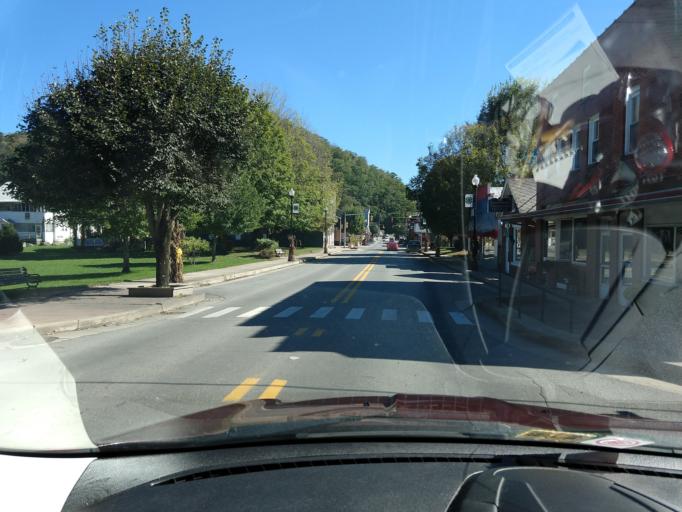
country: US
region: West Virginia
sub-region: Pocahontas County
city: Marlinton
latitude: 38.2242
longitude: -80.0954
